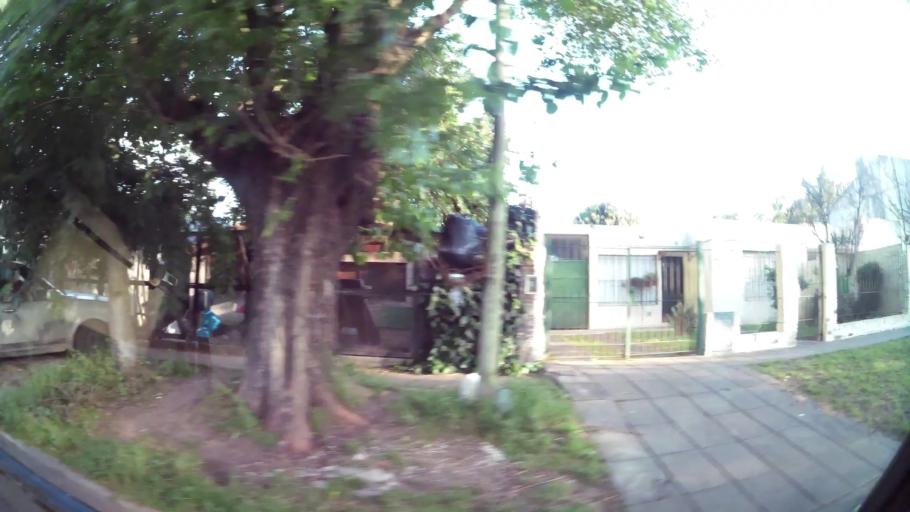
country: AR
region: Buenos Aires
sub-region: Partido de Tigre
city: Tigre
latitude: -34.4556
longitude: -58.6370
